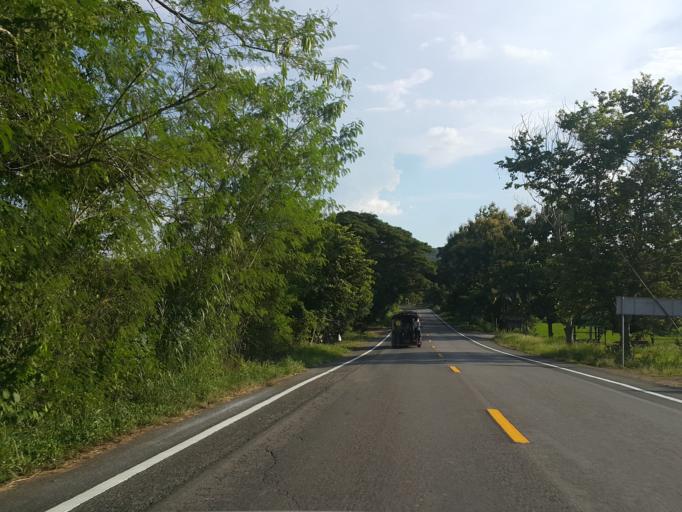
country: TH
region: Chiang Mai
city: Mae Taeng
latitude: 19.1033
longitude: 99.0004
